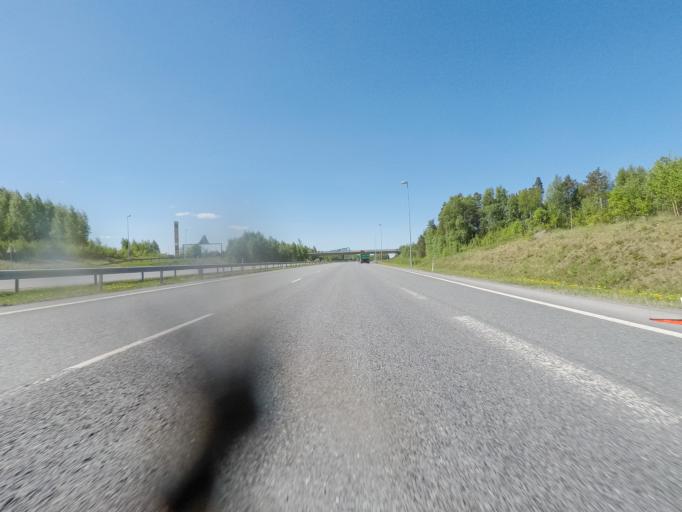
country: FI
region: Pirkanmaa
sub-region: Etelae-Pirkanmaa
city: Akaa
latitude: 61.1811
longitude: 23.8938
